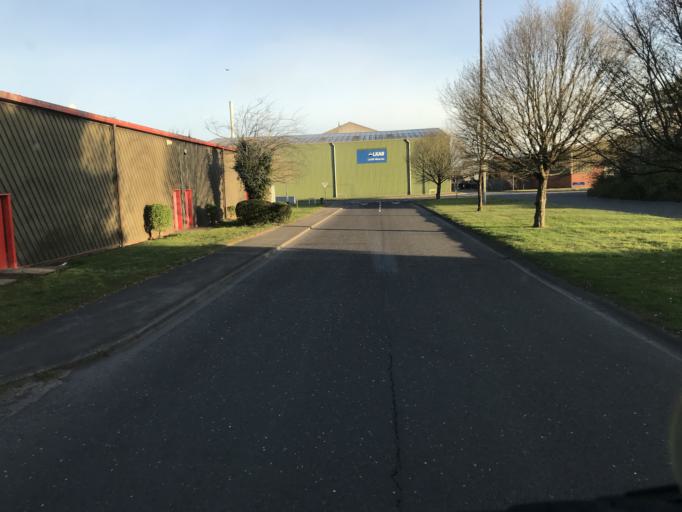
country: GB
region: England
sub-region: North Lincolnshire
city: Burton upon Stather
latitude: 53.6201
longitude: -0.6981
